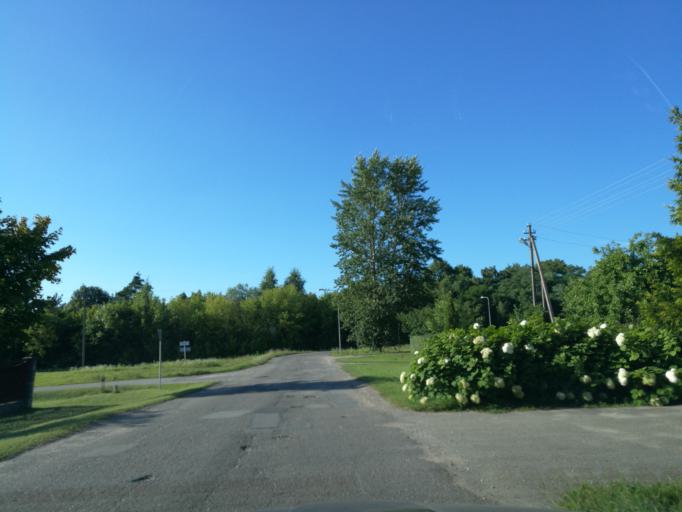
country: LT
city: Trakai
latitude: 54.6090
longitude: 24.9749
